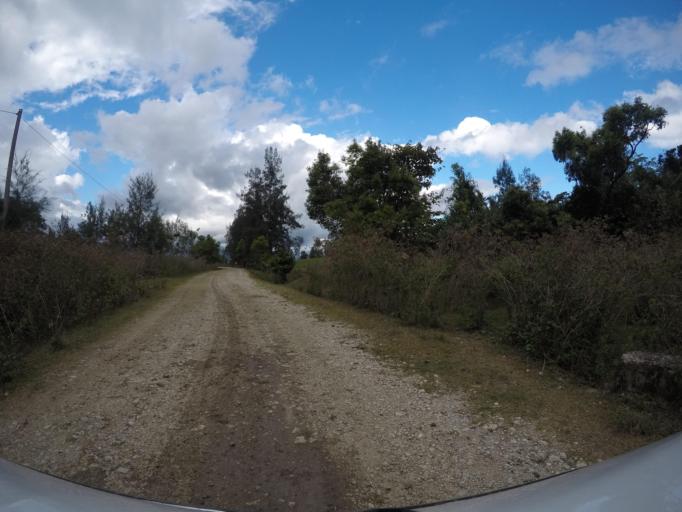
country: TL
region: Baucau
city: Venilale
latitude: -8.6812
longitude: 126.6444
